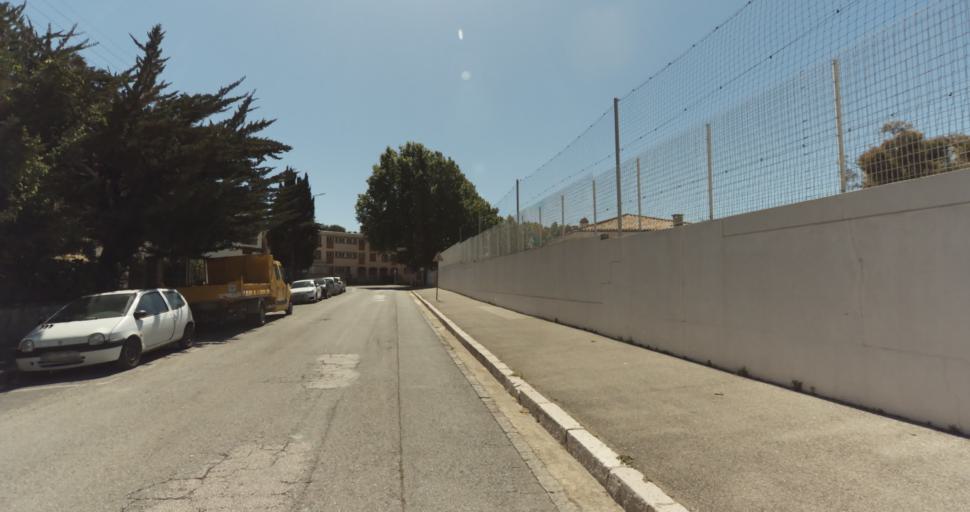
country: FR
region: Provence-Alpes-Cote d'Azur
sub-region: Departement du Var
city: Toulon
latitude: 43.1131
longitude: 5.9422
